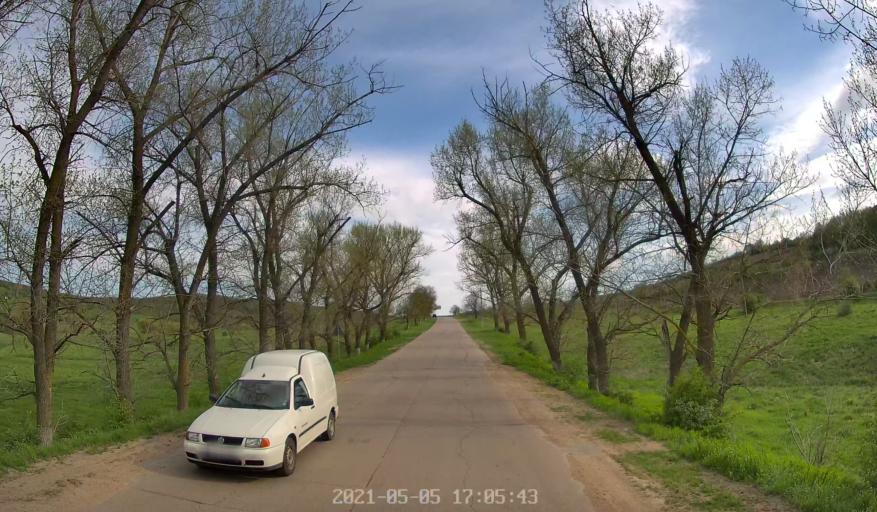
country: MD
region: Chisinau
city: Vadul lui Voda
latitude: 47.0272
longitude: 29.1393
